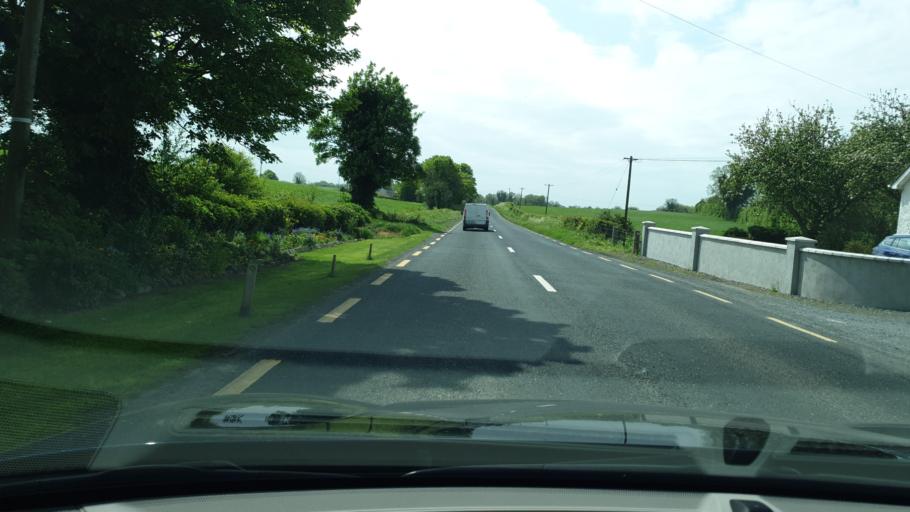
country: IE
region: Leinster
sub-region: An Mhi
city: Navan
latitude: 53.7665
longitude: -6.7252
